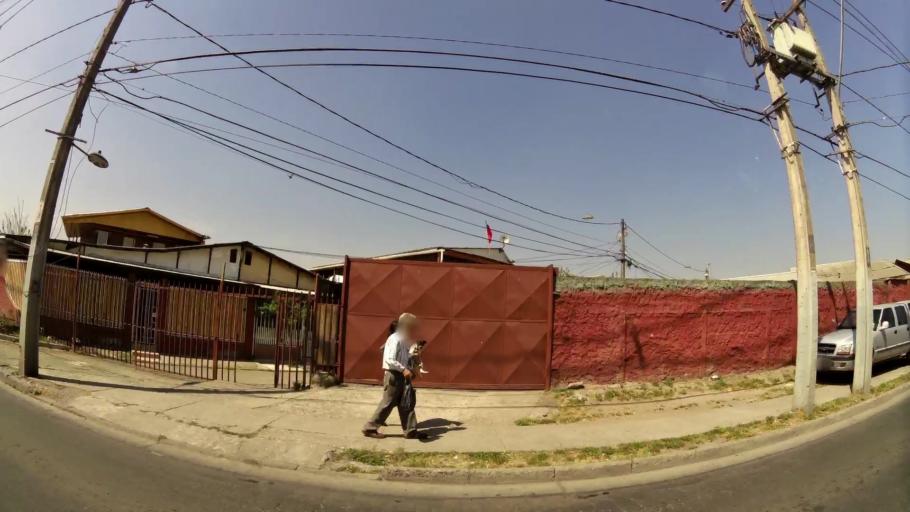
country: CL
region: Santiago Metropolitan
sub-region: Provincia de Santiago
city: La Pintana
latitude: -33.5544
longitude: -70.6112
